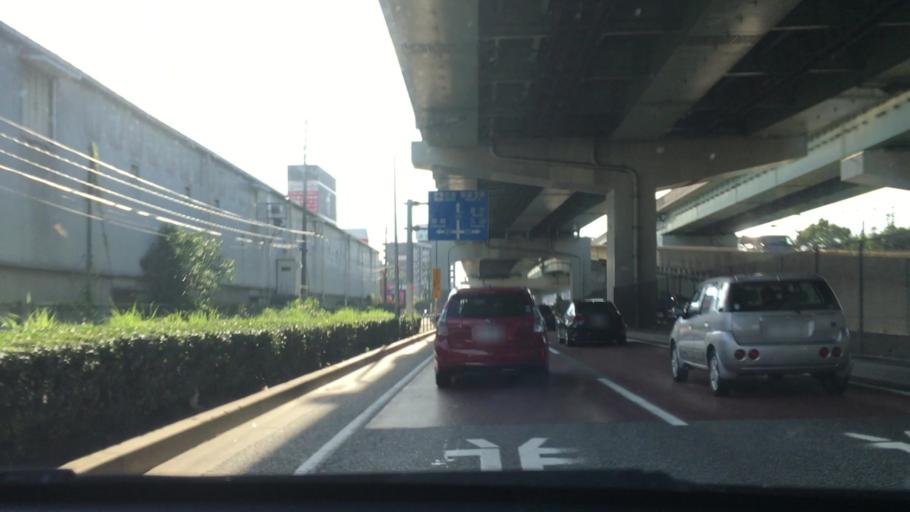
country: JP
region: Fukuoka
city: Fukuoka-shi
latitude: 33.6284
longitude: 130.4481
